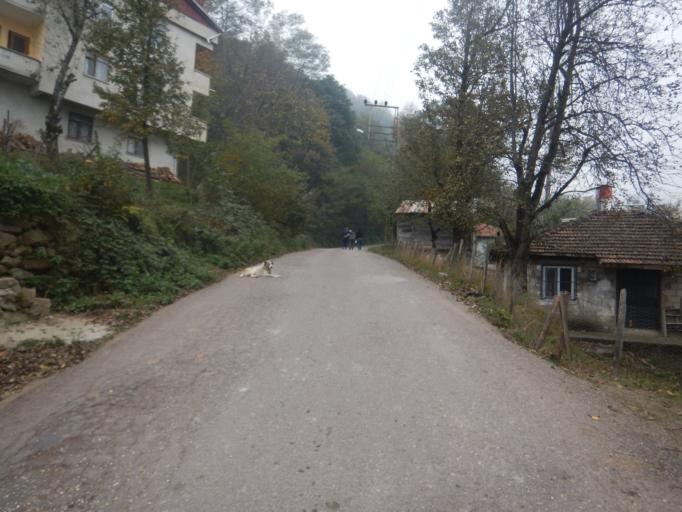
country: TR
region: Ordu
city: Golkoy
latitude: 40.6789
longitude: 37.5621
